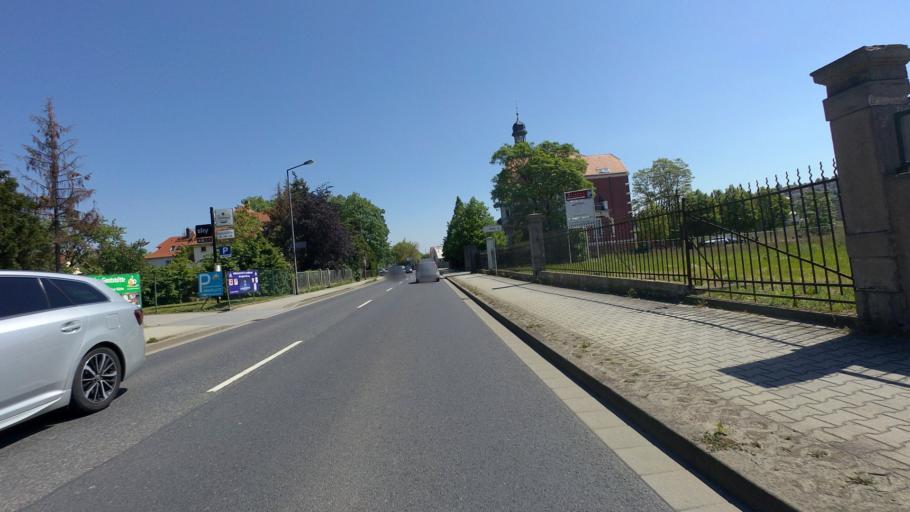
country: DE
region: Saxony
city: Radebeul
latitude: 51.0867
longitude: 13.6405
